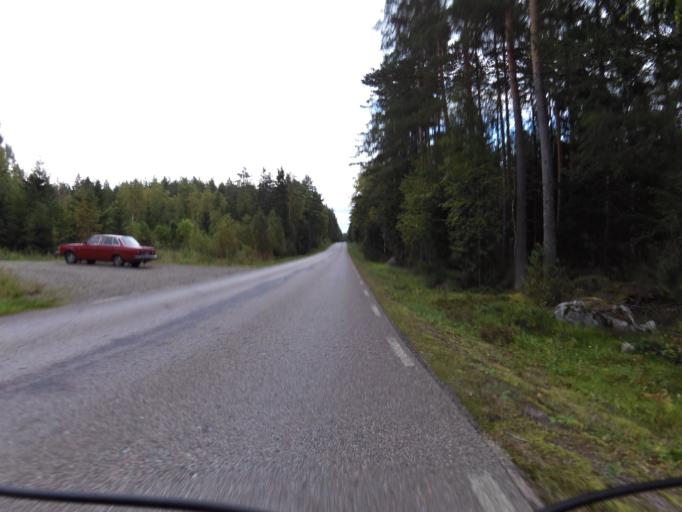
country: SE
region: Gaevleborg
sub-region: Sandvikens Kommun
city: Sandviken
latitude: 60.6522
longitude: 16.8313
